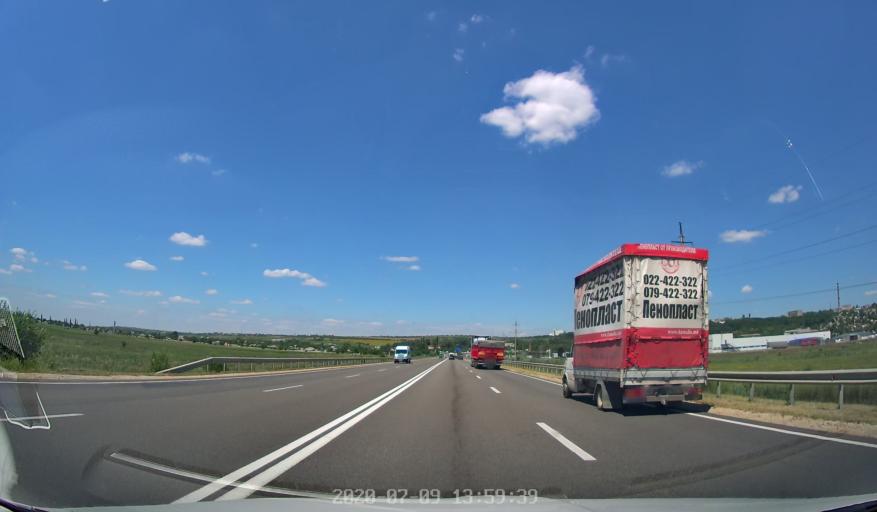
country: MD
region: Orhei
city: Orhei
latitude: 47.3793
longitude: 28.7962
